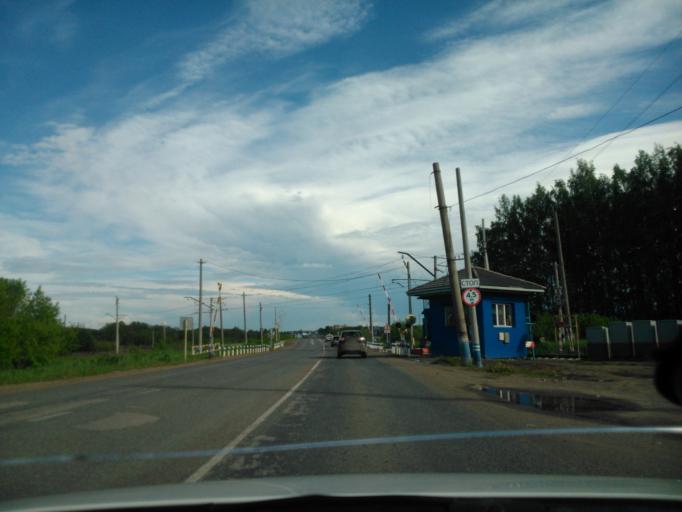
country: RU
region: Perm
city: Lobanovo
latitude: 57.8786
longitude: 56.2708
